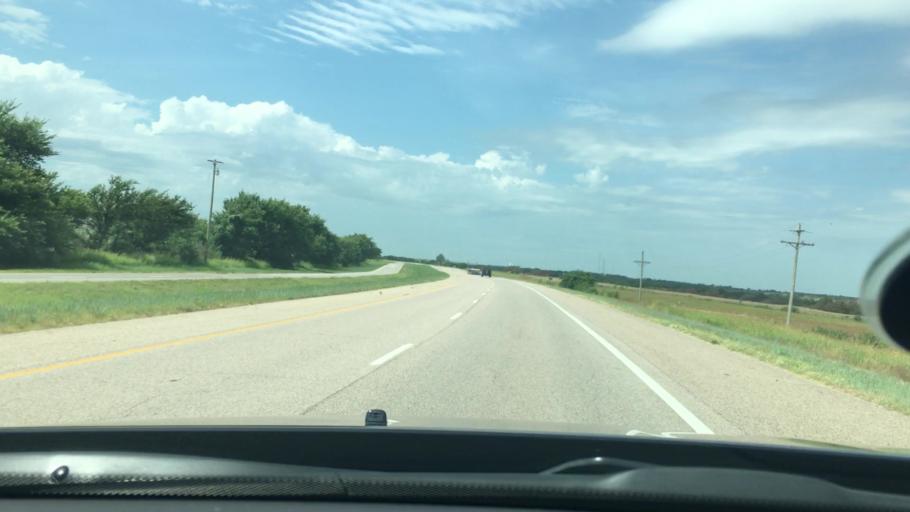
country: US
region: Oklahoma
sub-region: Pontotoc County
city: Ada
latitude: 34.7153
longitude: -96.7253
